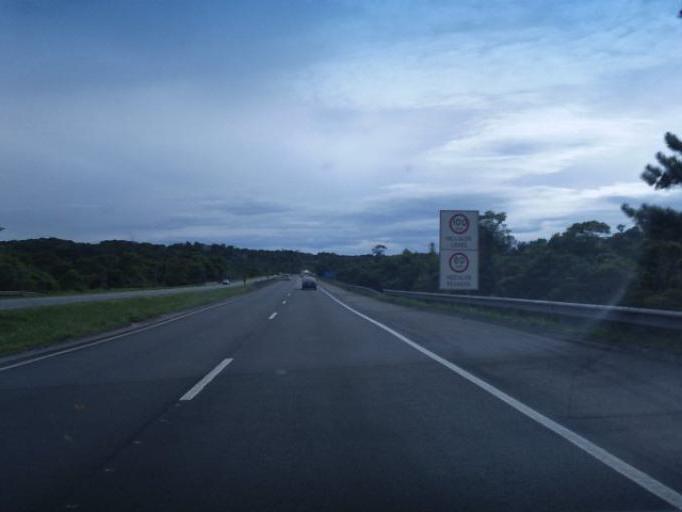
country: BR
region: Sao Paulo
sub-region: Cajati
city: Cajati
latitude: -24.9174
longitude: -48.2572
